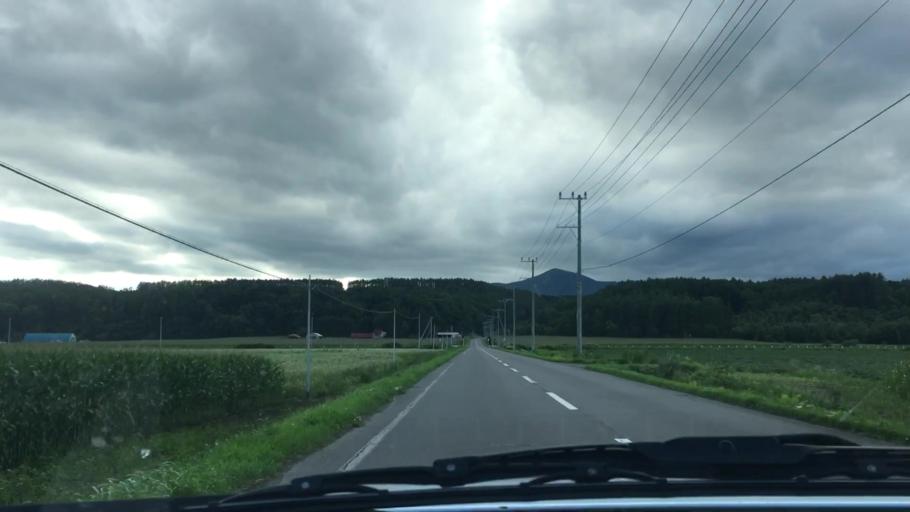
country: JP
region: Hokkaido
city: Otofuke
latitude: 43.1400
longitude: 142.8925
